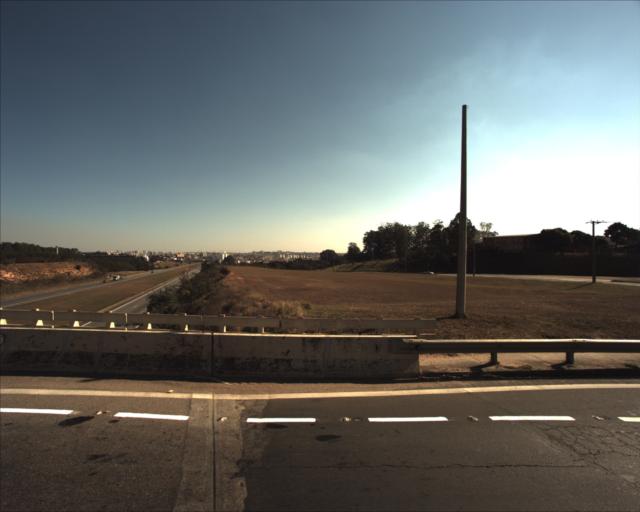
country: BR
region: Sao Paulo
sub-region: Sorocaba
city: Sorocaba
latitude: -23.4690
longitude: -47.4240
